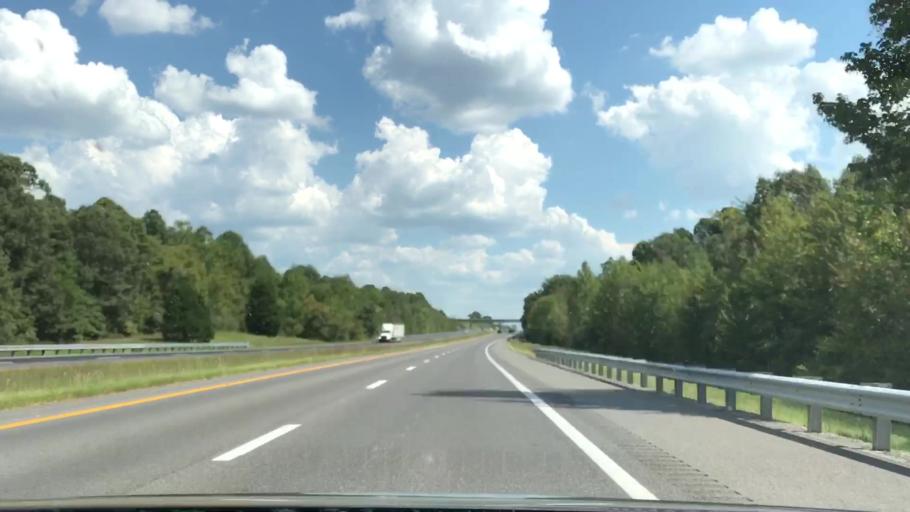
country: US
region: Kentucky
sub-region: Lyon County
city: Eddyville
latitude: 37.1090
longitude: -88.0073
